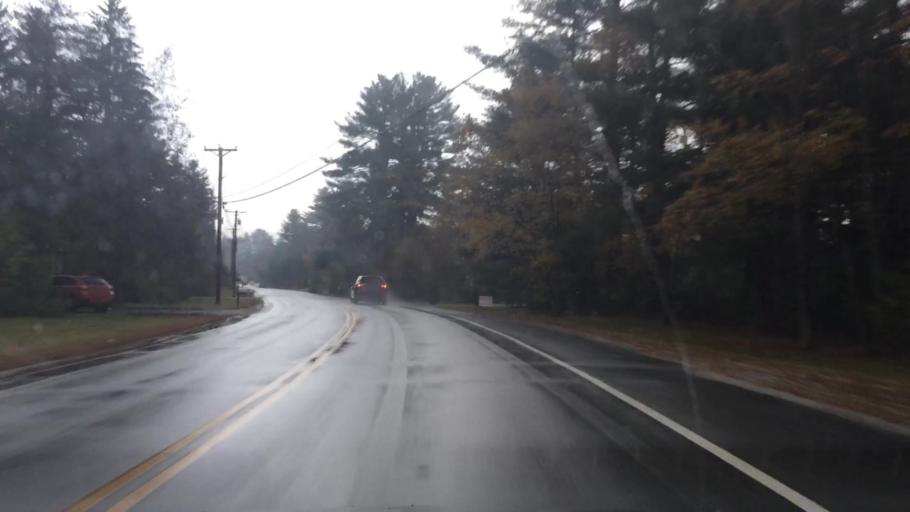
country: US
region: New Hampshire
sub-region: Cheshire County
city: Swanzey
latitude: 42.8646
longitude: -72.2802
